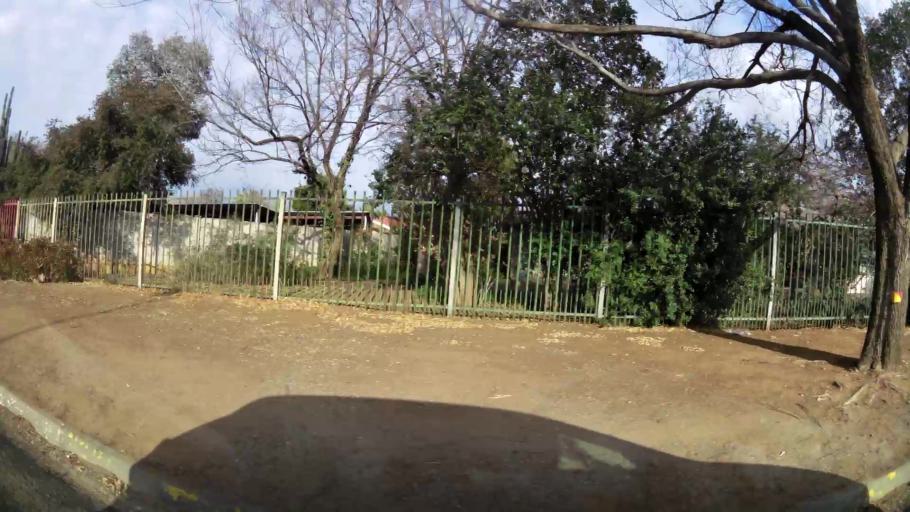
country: ZA
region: Orange Free State
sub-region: Mangaung Metropolitan Municipality
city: Bloemfontein
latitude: -29.1228
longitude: 26.1739
